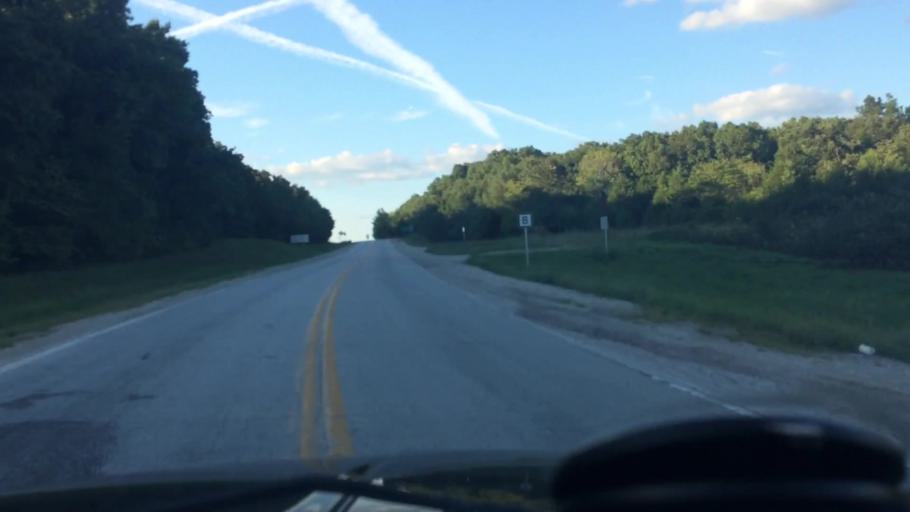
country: US
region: Missouri
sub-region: Webster County
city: Marshfield
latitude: 37.2976
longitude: -93.0010
